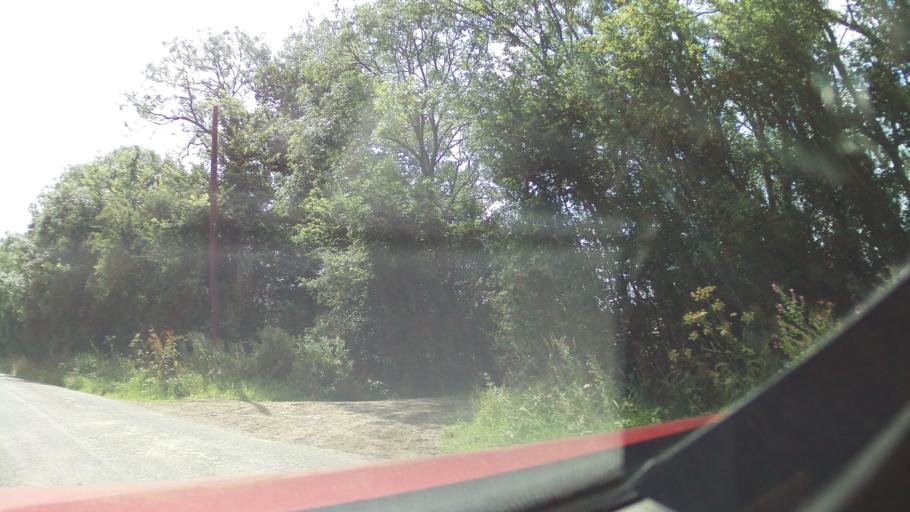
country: GB
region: England
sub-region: Wiltshire
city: Minety
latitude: 51.6096
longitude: -1.9556
